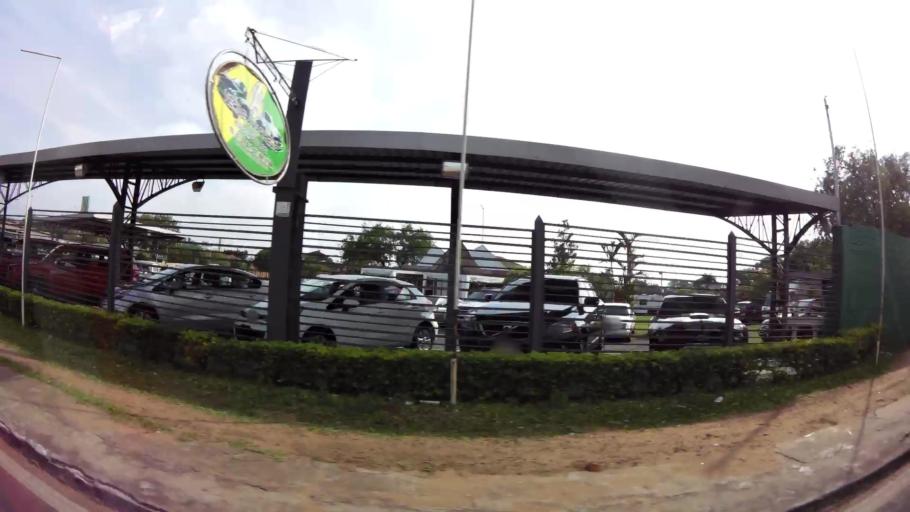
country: PY
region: Central
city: Fernando de la Mora
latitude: -25.3080
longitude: -57.5522
